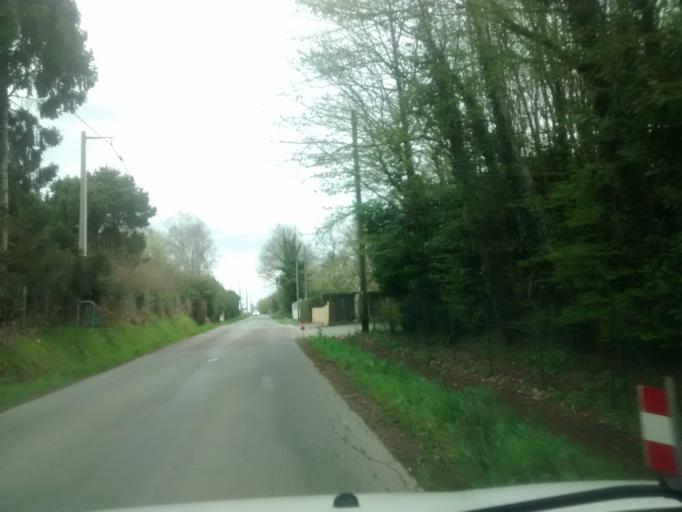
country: FR
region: Brittany
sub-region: Departement d'Ille-et-Vilaine
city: Saint-Sulpice-la-Foret
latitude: 48.1982
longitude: -1.5987
